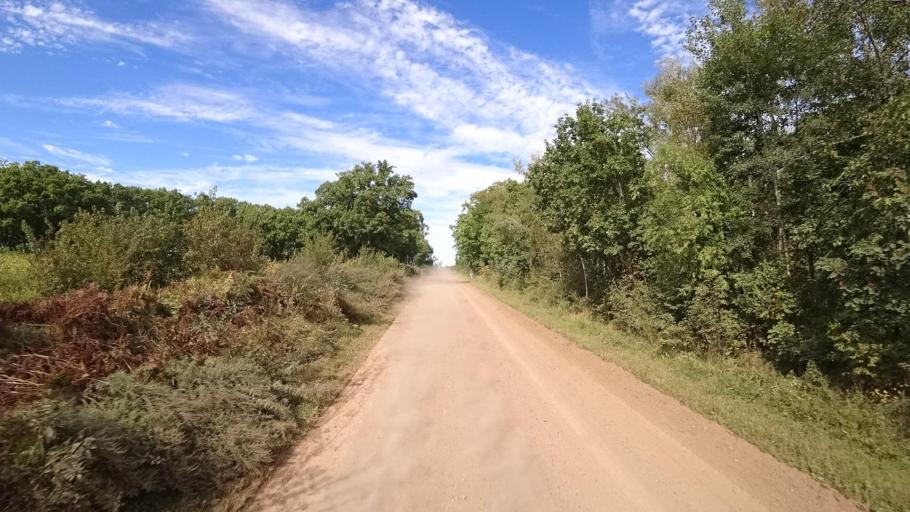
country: RU
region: Primorskiy
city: Dostoyevka
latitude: 44.3784
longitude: 133.5331
